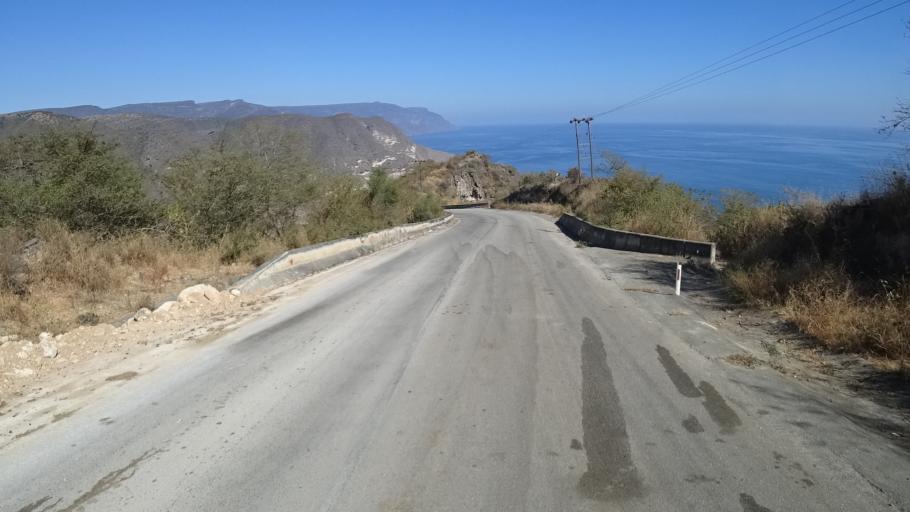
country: YE
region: Al Mahrah
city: Hawf
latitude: 16.7455
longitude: 53.4019
